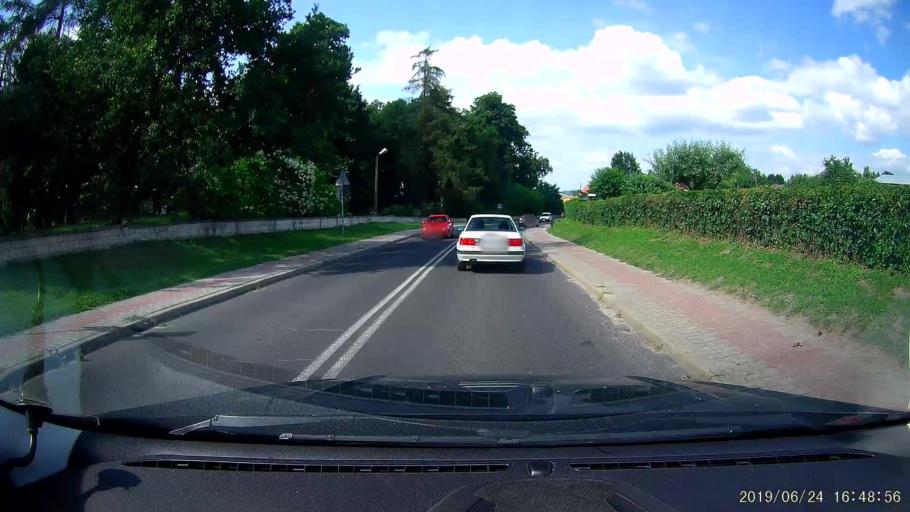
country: PL
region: Lublin Voivodeship
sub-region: Powiat tomaszowski
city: Laszczow
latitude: 50.5320
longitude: 23.7191
